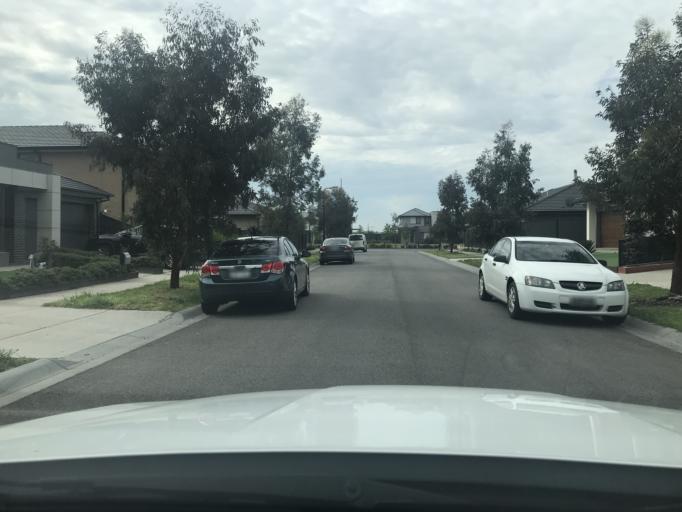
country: AU
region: Victoria
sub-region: Hume
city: Roxburgh Park
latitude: -37.6023
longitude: 144.9020
